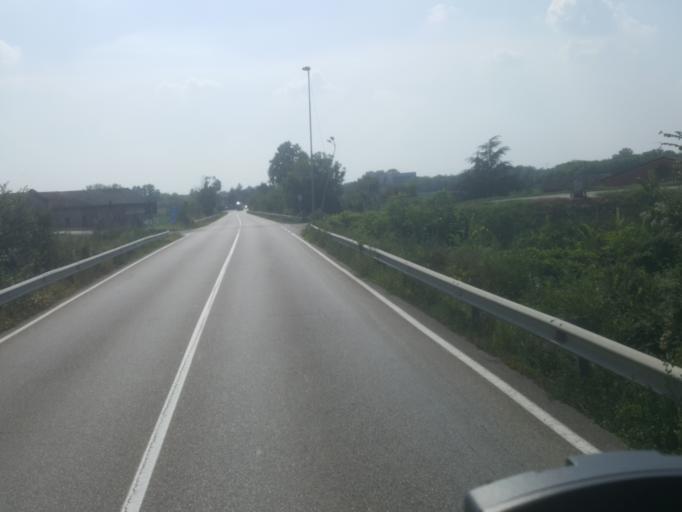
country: IT
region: Lombardy
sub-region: Provincia di Cremona
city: Casalmaggiore
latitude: 44.9661
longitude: 10.4027
